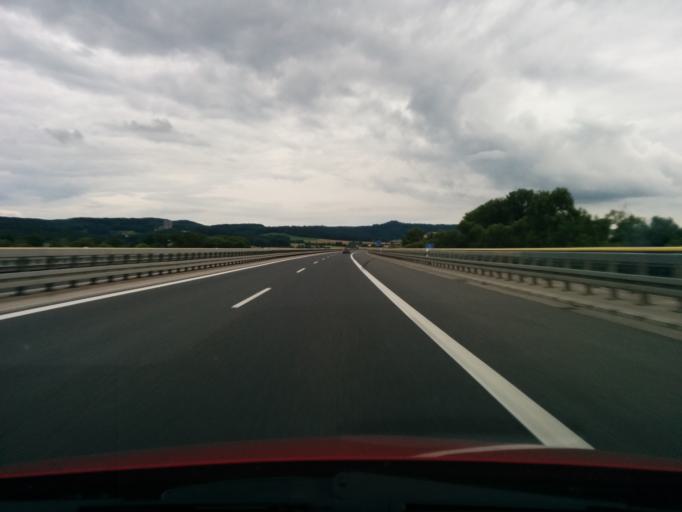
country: DE
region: Bavaria
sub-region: Upper Franconia
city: Lichtenfels
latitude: 50.1406
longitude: 11.0341
